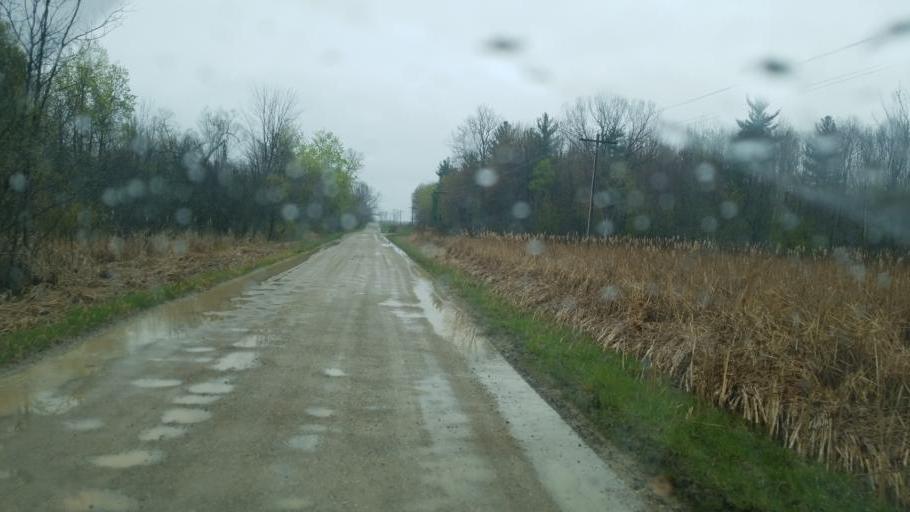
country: US
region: Michigan
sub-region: Montcalm County
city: Lakeview
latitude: 43.4739
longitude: -85.2937
